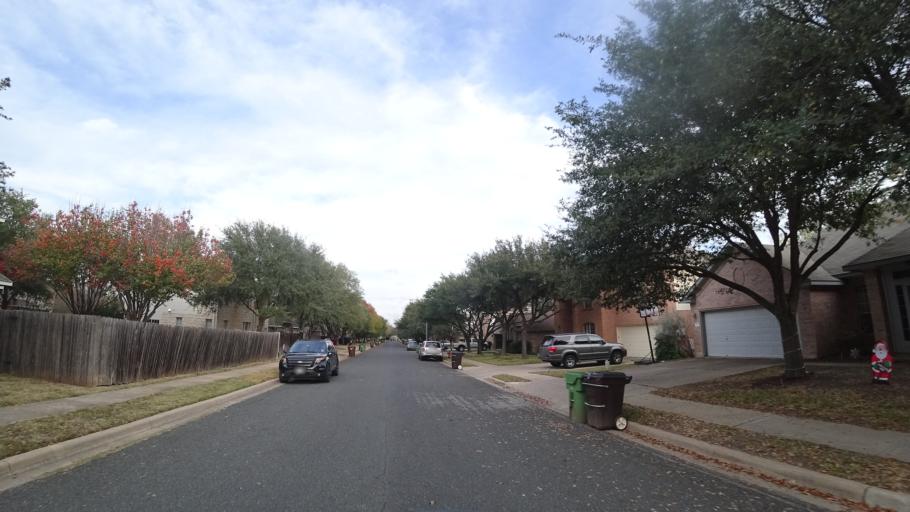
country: US
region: Texas
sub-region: Williamson County
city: Brushy Creek
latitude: 30.5137
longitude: -97.7231
